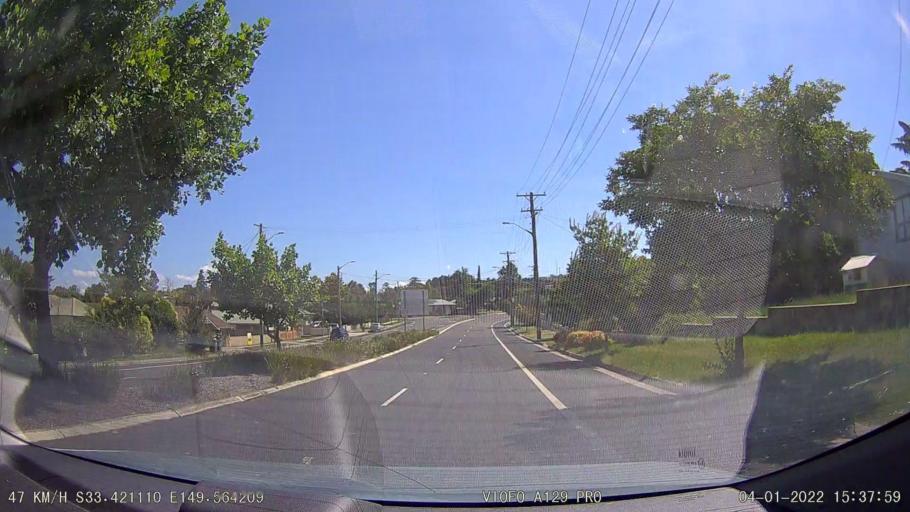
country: AU
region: New South Wales
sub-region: Bathurst Regional
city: Bathurst
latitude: -33.4209
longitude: 149.5645
